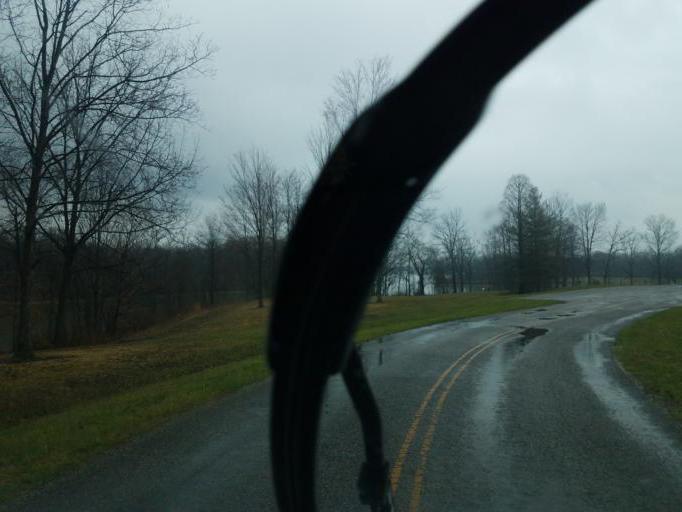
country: US
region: Ohio
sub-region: Delaware County
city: Lewis Center
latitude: 40.2006
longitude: -82.9770
